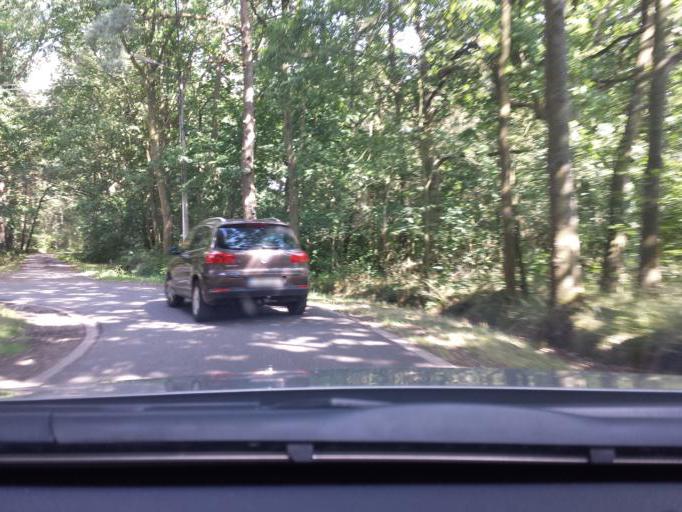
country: BE
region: Flanders
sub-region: Provincie Limburg
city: Lummen
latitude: 50.9825
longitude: 5.2247
